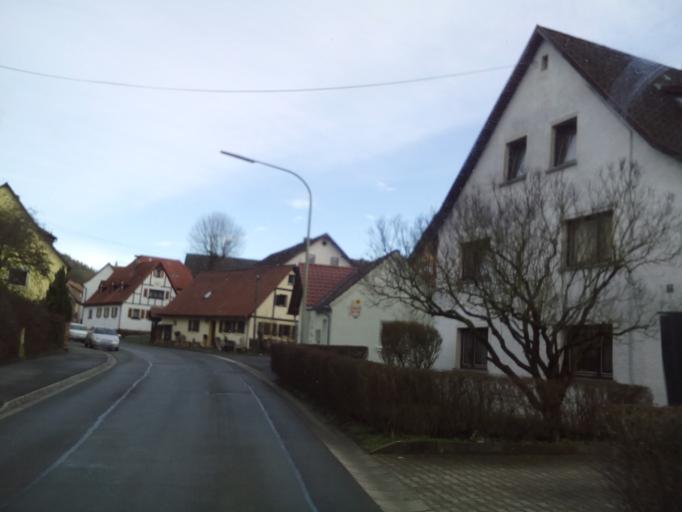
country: DE
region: Bavaria
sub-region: Upper Franconia
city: Kodnitz
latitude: 50.1085
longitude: 11.5132
